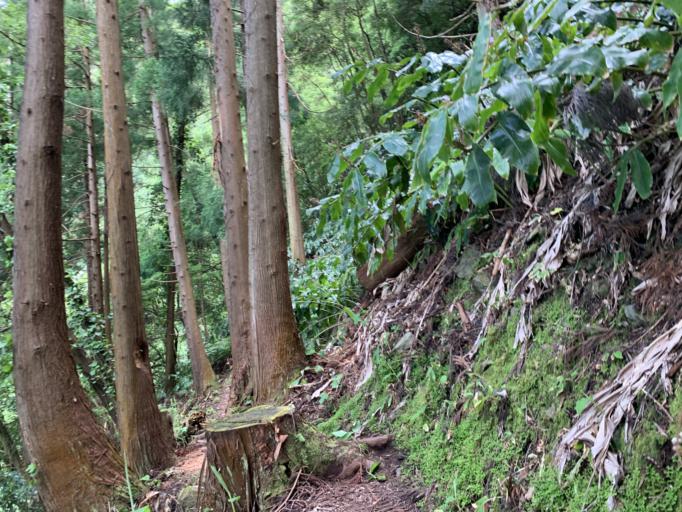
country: PT
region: Azores
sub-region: Ponta Delgada
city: Arrifes
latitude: 37.8414
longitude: -25.7890
